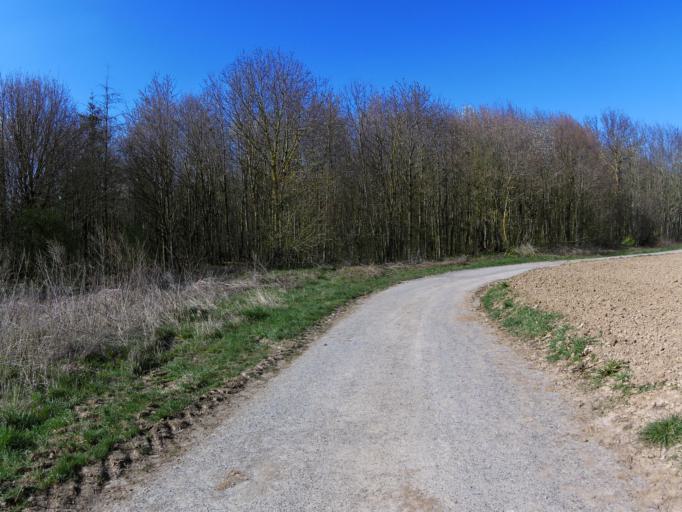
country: DE
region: Bavaria
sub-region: Regierungsbezirk Unterfranken
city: Biebelried
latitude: 49.7711
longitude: 10.0939
